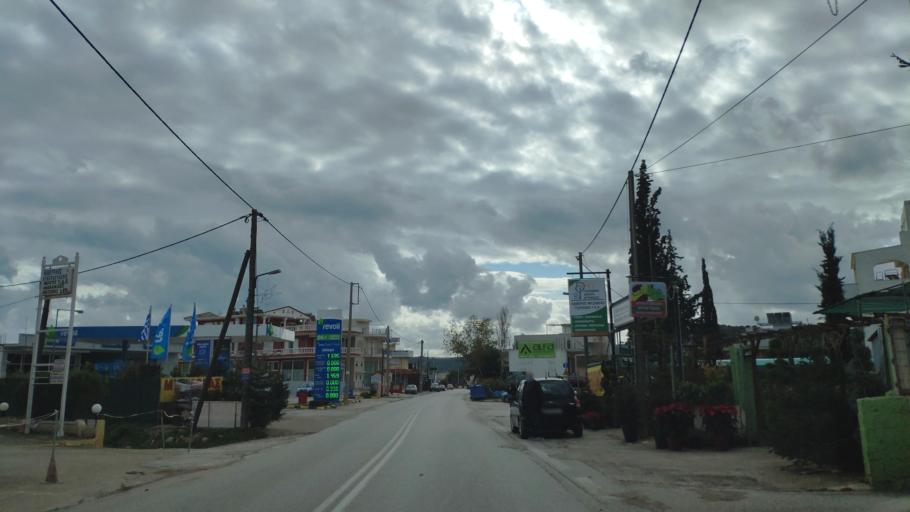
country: GR
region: Attica
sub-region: Nomarchia Anatolikis Attikis
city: Artemida
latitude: 37.9449
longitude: 24.0078
